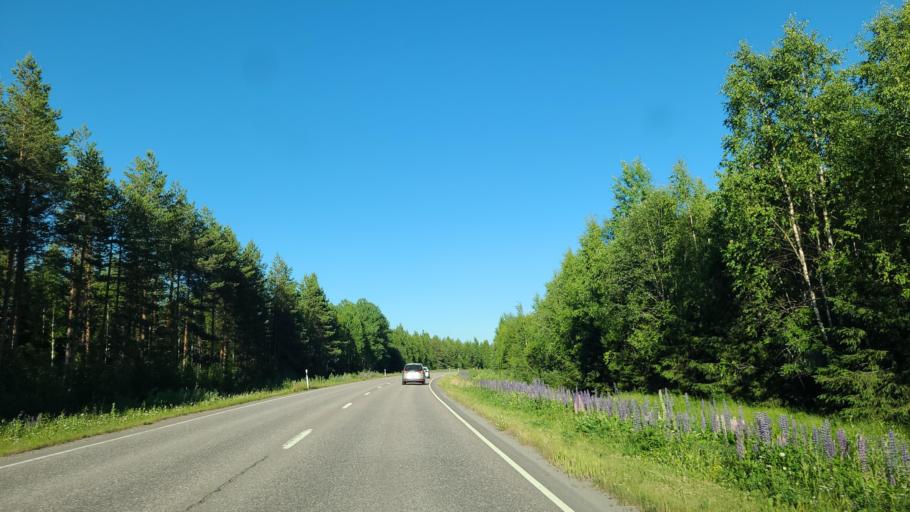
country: FI
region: Southern Savonia
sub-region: Pieksaemaeki
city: Jaeppilae
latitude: 62.2890
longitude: 27.4687
